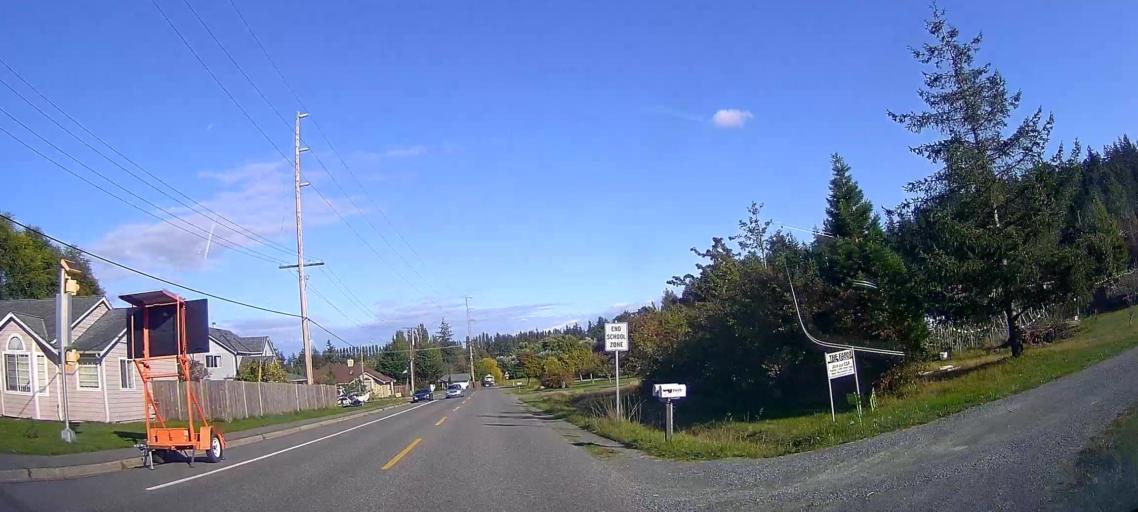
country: US
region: Washington
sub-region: Skagit County
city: Anacortes
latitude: 48.4878
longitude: -122.6159
